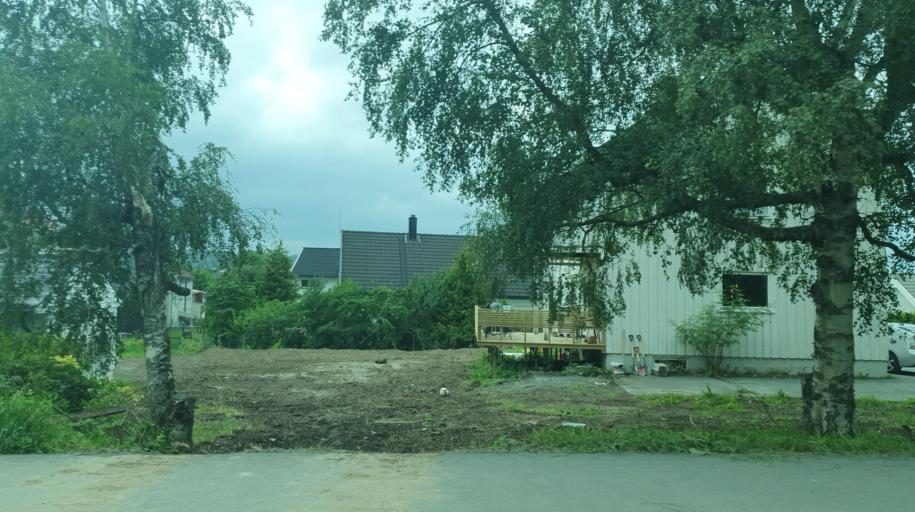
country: NO
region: Sor-Trondelag
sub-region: Trondheim
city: Trondheim
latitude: 63.3587
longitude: 10.3664
